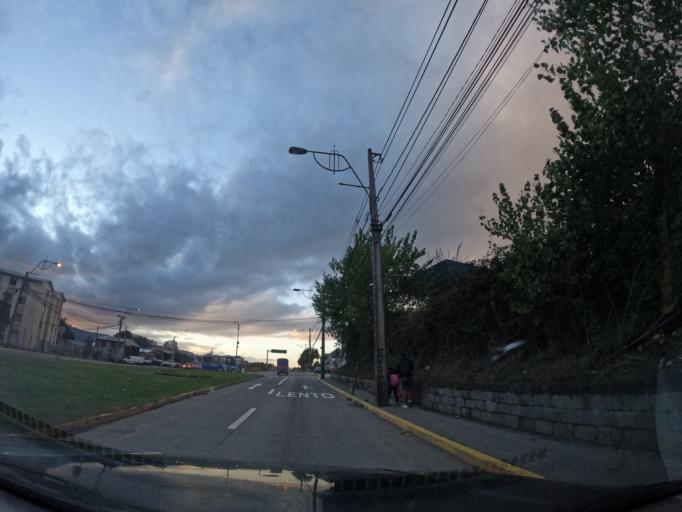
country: CL
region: Biobio
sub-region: Provincia de Concepcion
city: Chiguayante
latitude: -36.9587
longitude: -73.0118
